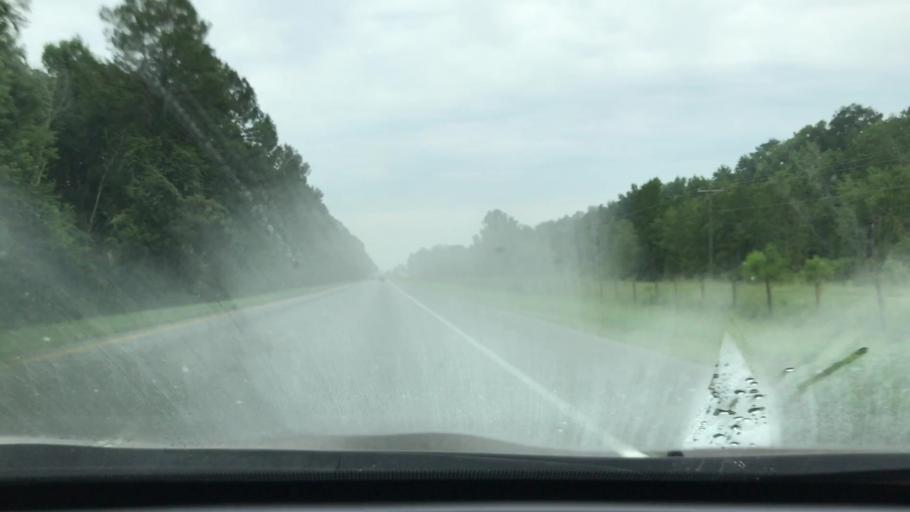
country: US
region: South Carolina
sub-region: Jasper County
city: Ridgeland
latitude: 32.5385
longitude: -80.9546
